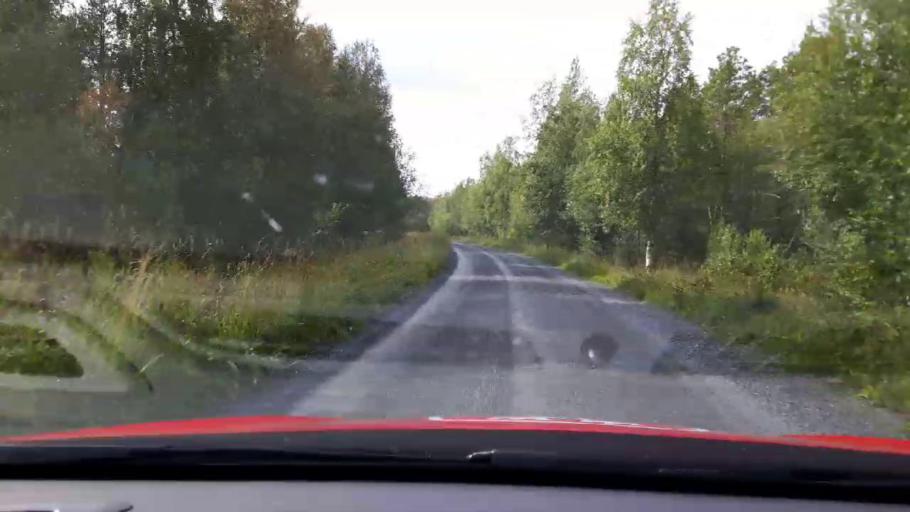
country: SE
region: Jaemtland
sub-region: Krokoms Kommun
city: Valla
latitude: 63.2620
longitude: 13.8328
